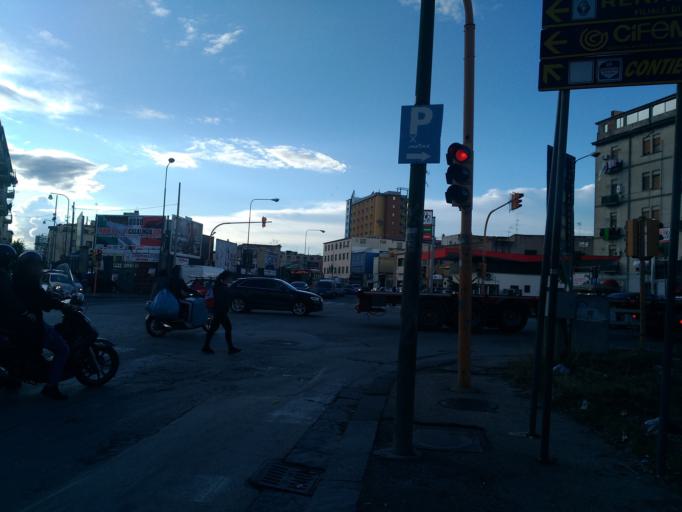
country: IT
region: Campania
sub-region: Provincia di Napoli
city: Napoli
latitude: 40.8497
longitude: 14.2896
